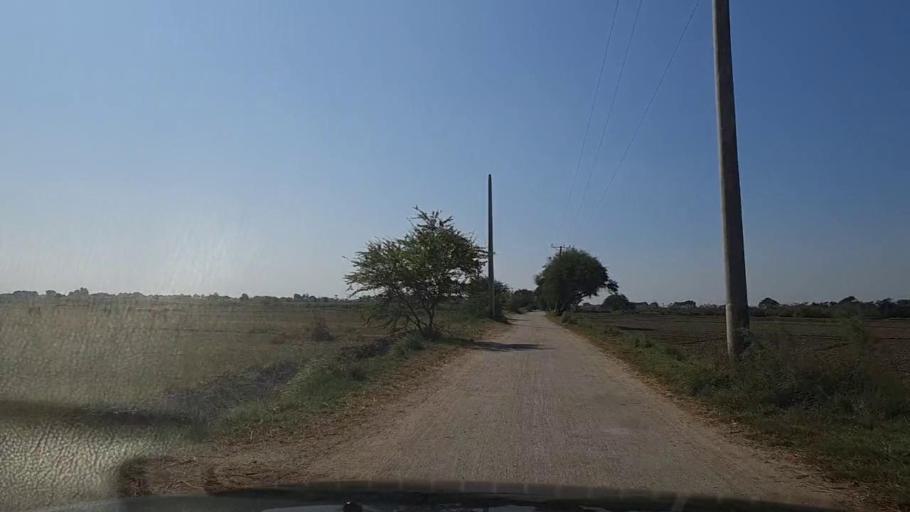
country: PK
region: Sindh
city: Mirpur Sakro
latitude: 24.6054
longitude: 67.7918
